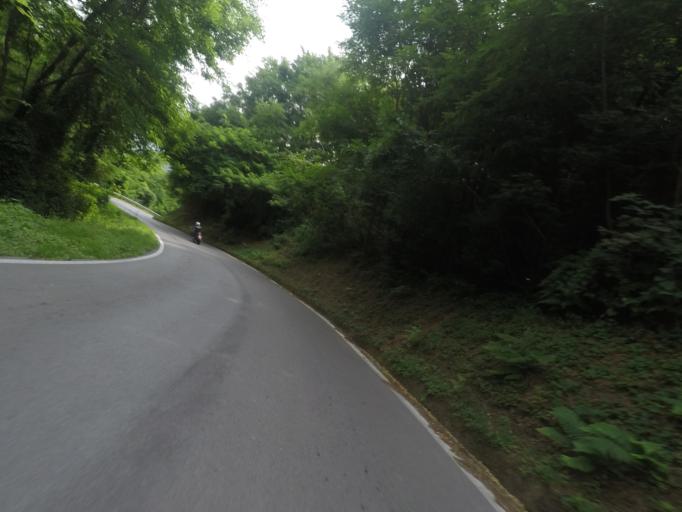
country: IT
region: Tuscany
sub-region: Provincia di Lucca
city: Castelnuovo di Garfagnana
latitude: 44.1091
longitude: 10.4048
